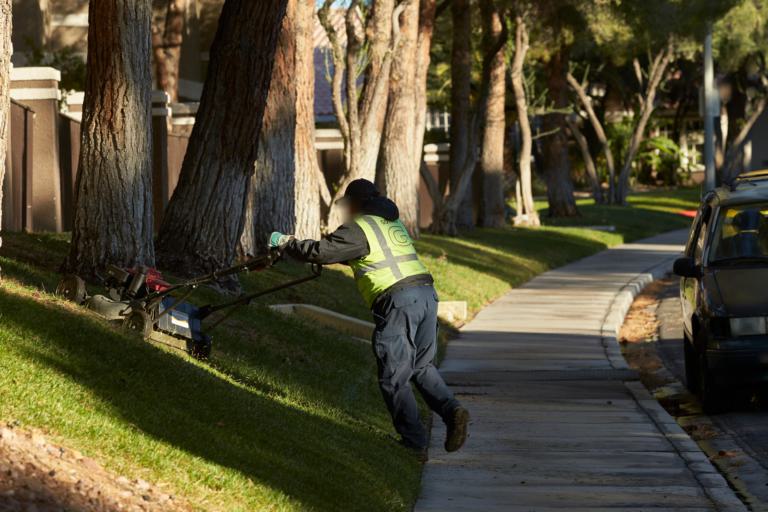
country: US
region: Nevada
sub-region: Clark County
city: Summerlin South
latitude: 36.1426
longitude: -115.3064
